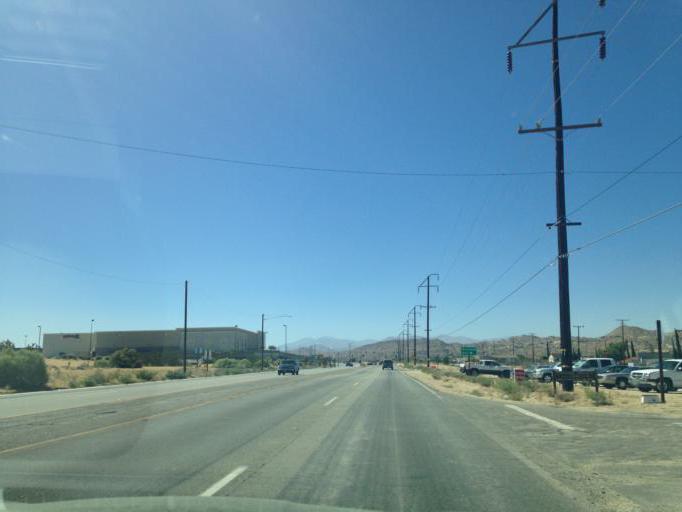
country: US
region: California
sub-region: San Bernardino County
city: Yucca Valley
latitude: 34.1350
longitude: -116.3785
